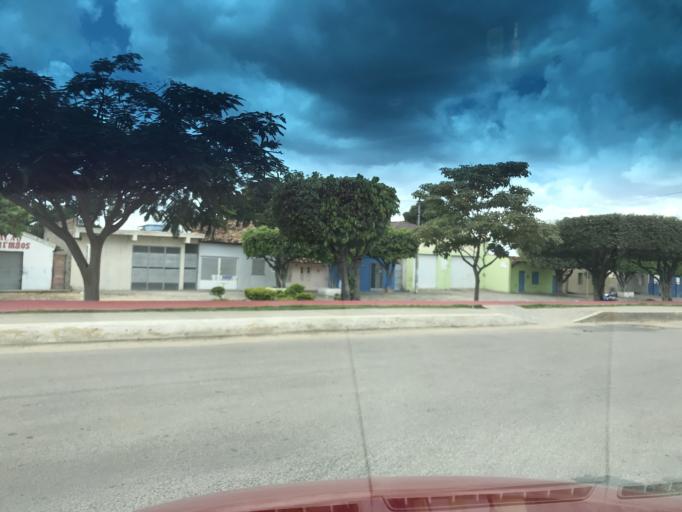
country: BR
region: Bahia
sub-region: Itaberaba
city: Itaberaba
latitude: -12.5188
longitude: -40.3058
